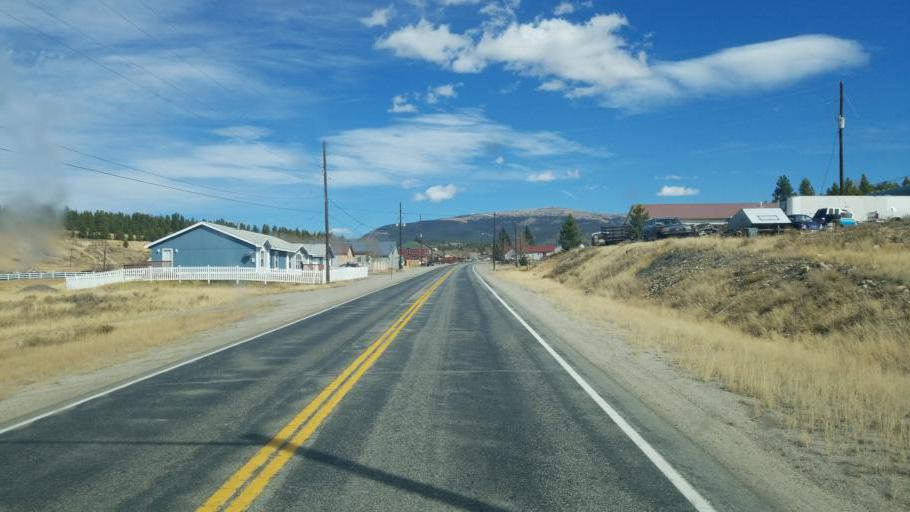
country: US
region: Colorado
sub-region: Lake County
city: Leadville North
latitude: 39.2342
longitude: -106.3178
